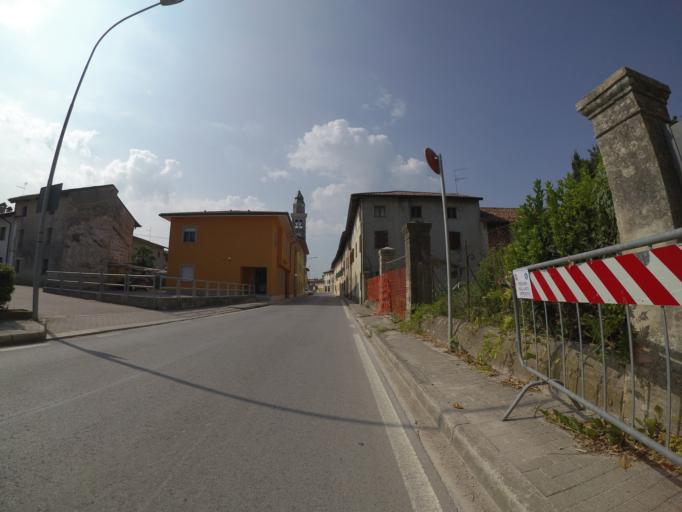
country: IT
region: Friuli Venezia Giulia
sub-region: Provincia di Udine
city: Palazzolo dello Stella
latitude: 45.8189
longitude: 13.0815
